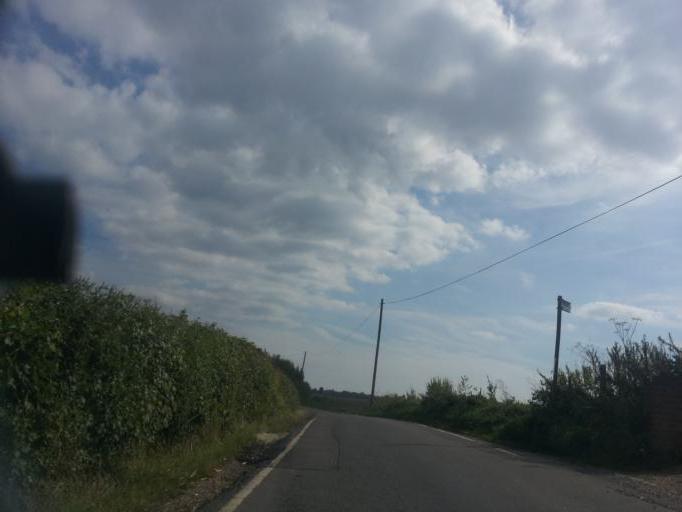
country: GB
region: England
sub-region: Kent
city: Boxley
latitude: 51.3401
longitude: 0.5554
